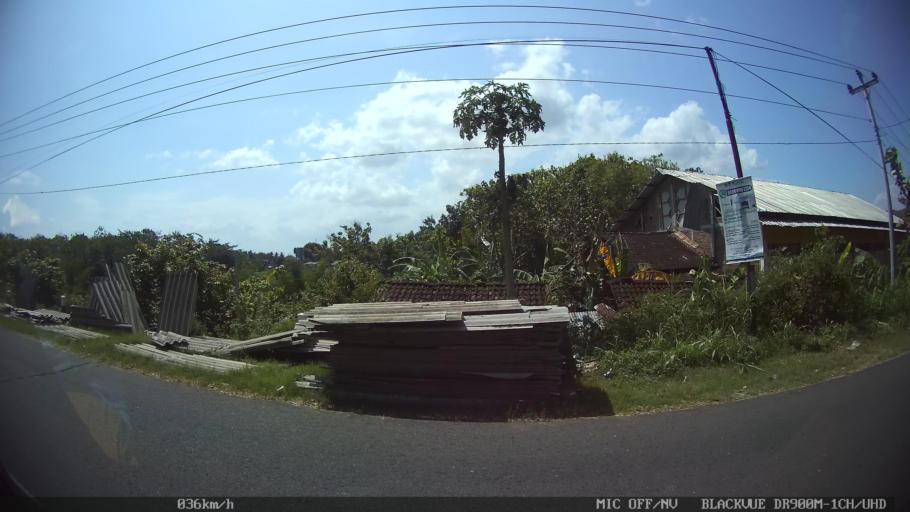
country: ID
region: Daerah Istimewa Yogyakarta
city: Pundong
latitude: -7.9531
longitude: 110.3800
